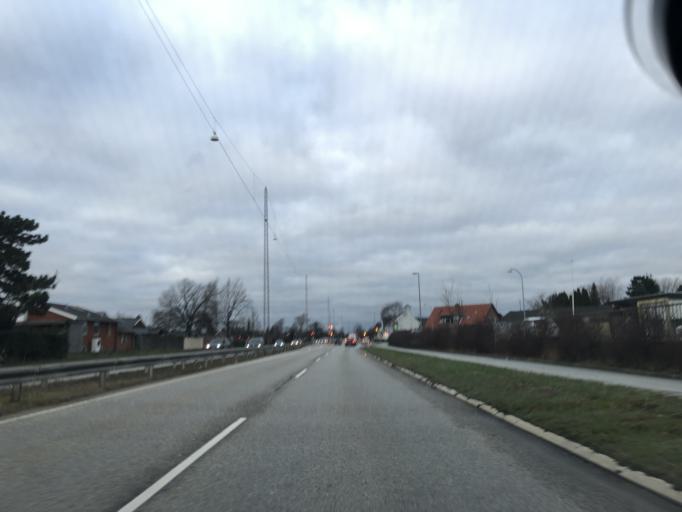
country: DK
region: Capital Region
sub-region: Hvidovre Kommune
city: Hvidovre
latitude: 55.6336
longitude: 12.4682
